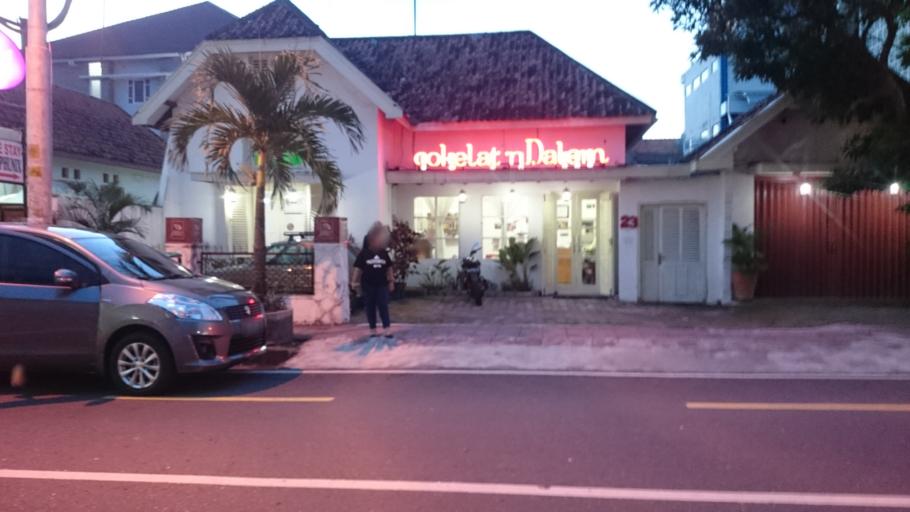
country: ID
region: Daerah Istimewa Yogyakarta
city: Yogyakarta
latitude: -7.7994
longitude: 110.3621
